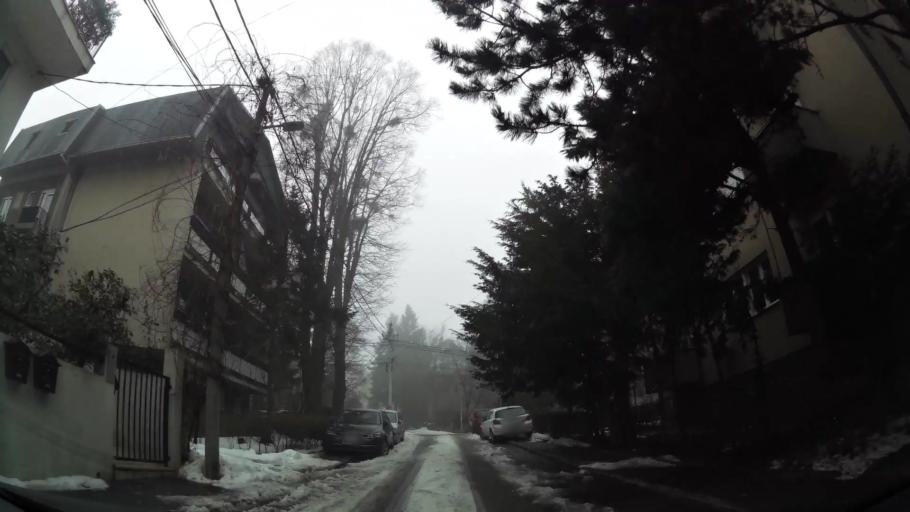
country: RS
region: Central Serbia
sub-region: Belgrade
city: Savski Venac
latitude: 44.7725
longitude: 20.4575
